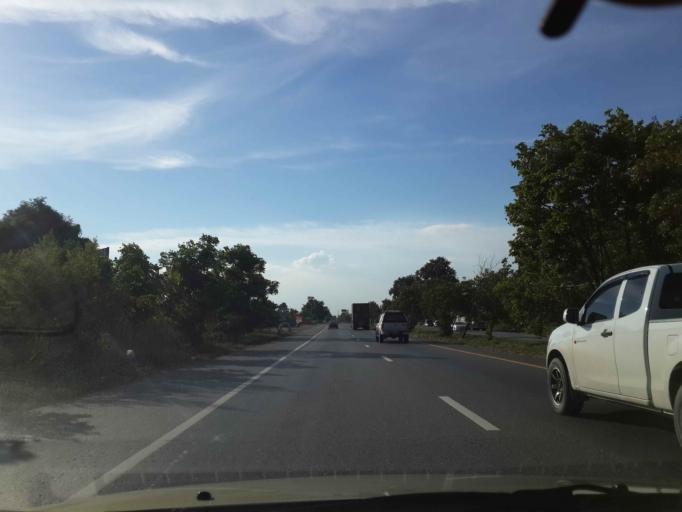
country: TH
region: Chon Buri
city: Phatthaya
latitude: 12.9375
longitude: 100.9970
